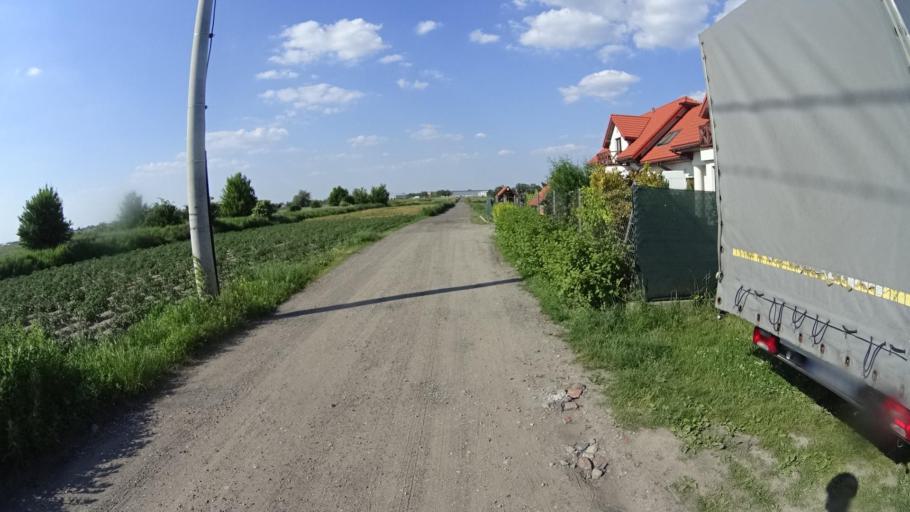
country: PL
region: Masovian Voivodeship
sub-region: Powiat warszawski zachodni
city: Ozarow Mazowiecki
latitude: 52.1943
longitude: 20.7638
